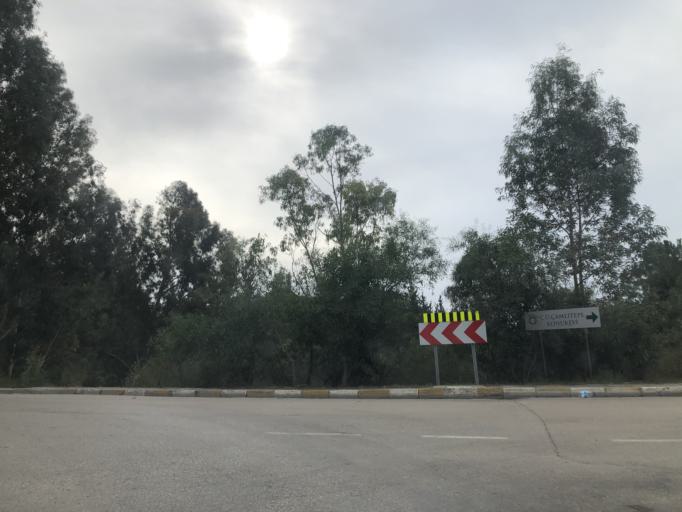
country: TR
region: Adana
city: Adana
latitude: 37.0577
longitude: 35.3527
